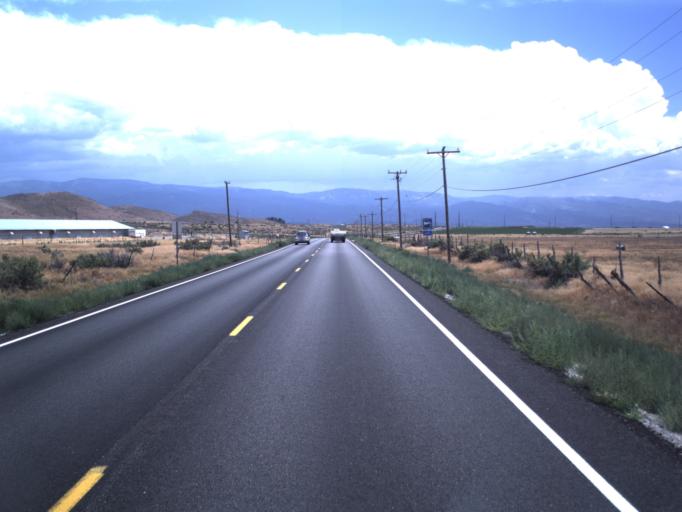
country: US
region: Utah
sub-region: Sanpete County
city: Moroni
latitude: 39.5632
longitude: -111.6035
